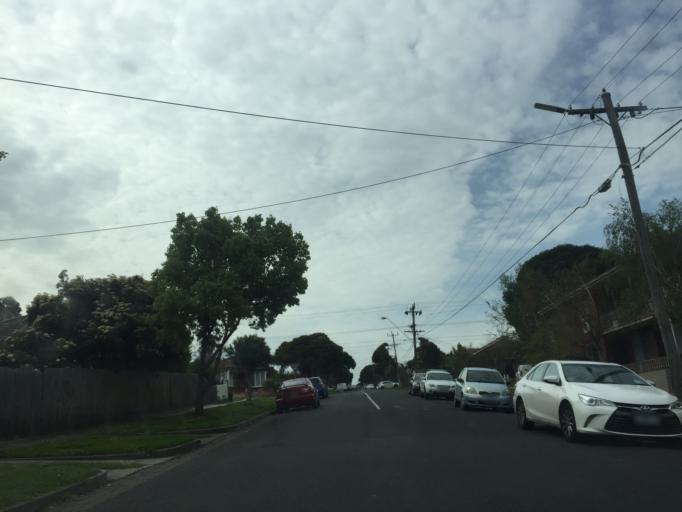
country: AU
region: Victoria
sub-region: Darebin
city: Preston
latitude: -37.7562
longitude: 145.0160
